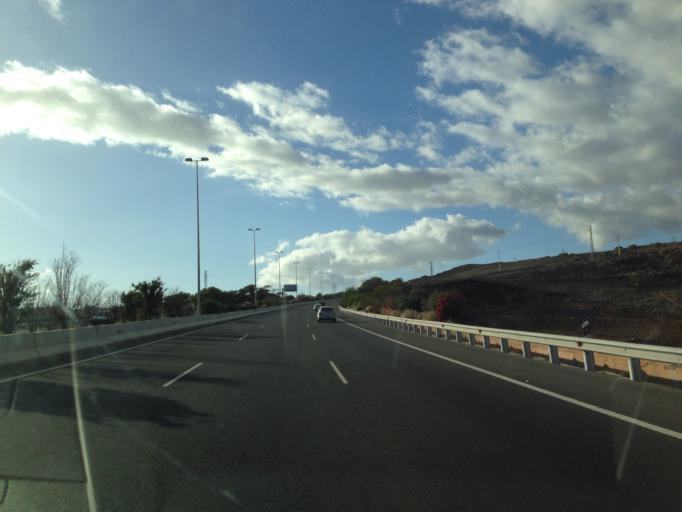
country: ES
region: Canary Islands
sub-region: Provincia de Las Palmas
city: Playa del Ingles
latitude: 27.7678
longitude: -15.5654
